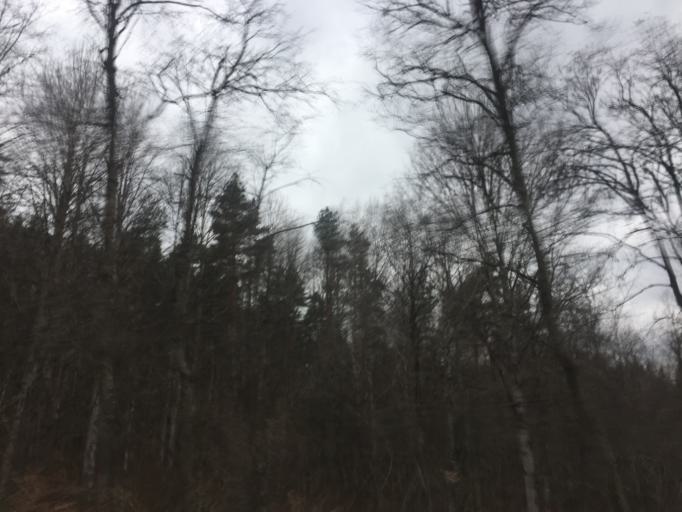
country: RU
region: Republic of Karelia
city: Lakhdenpokh'ya
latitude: 61.4331
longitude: 30.1461
